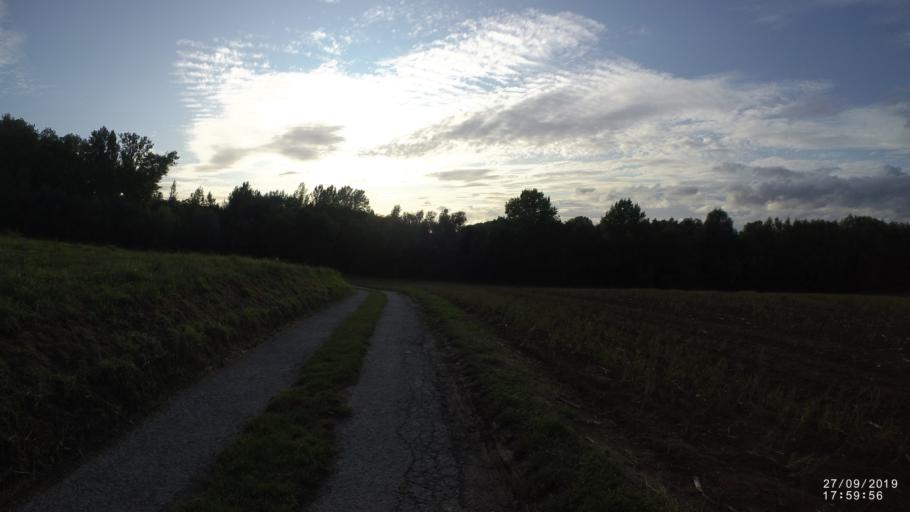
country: BE
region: Wallonia
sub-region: Province du Hainaut
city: Ellezelles
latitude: 50.8066
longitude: 3.6985
